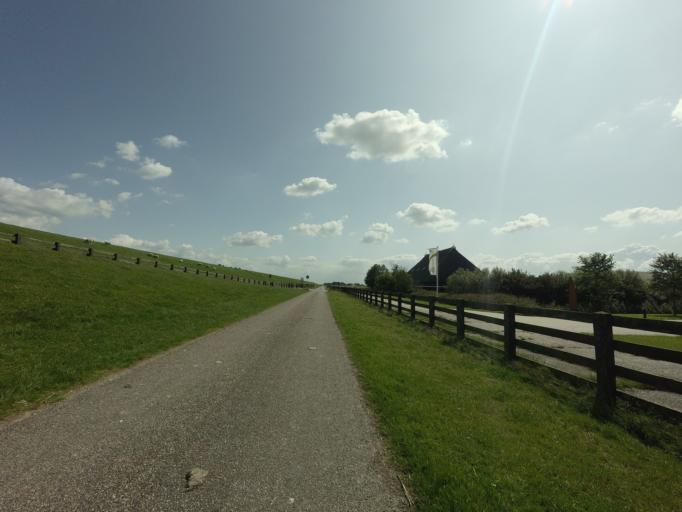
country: NL
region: Friesland
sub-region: Gemeente Ferwerderadiel
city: Hallum
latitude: 53.3231
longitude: 5.7399
